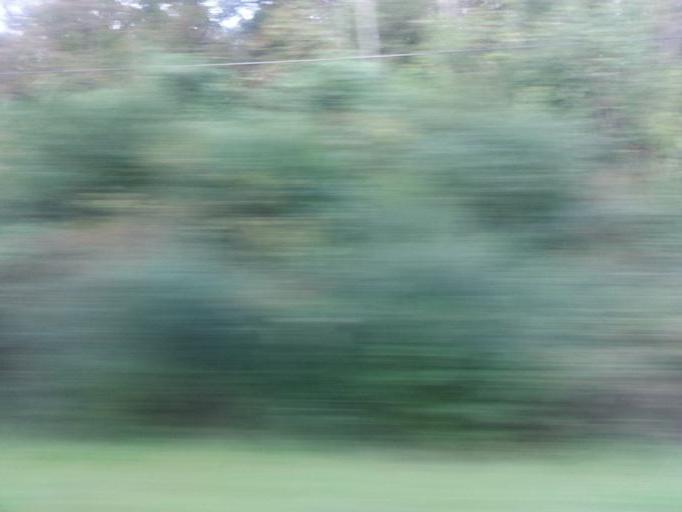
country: US
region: Tennessee
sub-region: Campbell County
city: Caryville
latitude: 36.2757
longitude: -84.2034
